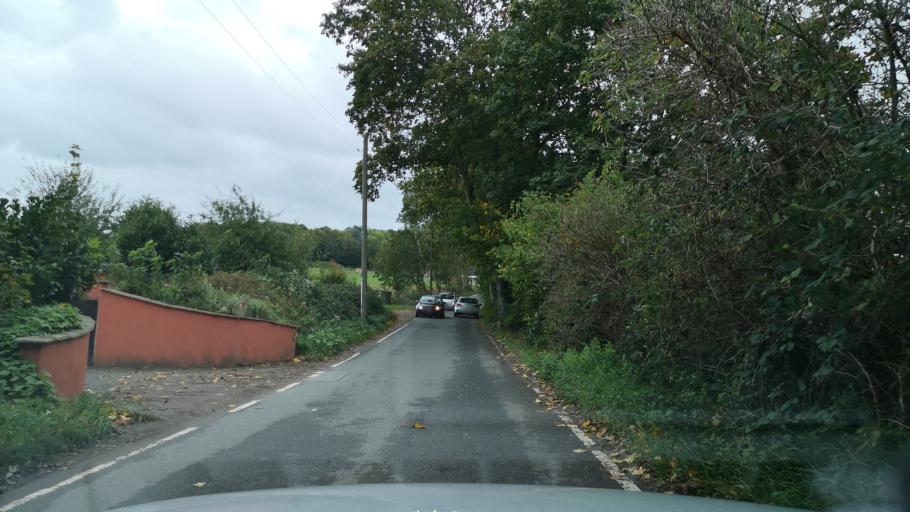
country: DE
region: North Rhine-Westphalia
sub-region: Regierungsbezirk Dusseldorf
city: Velbert
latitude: 51.3797
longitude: 7.0420
